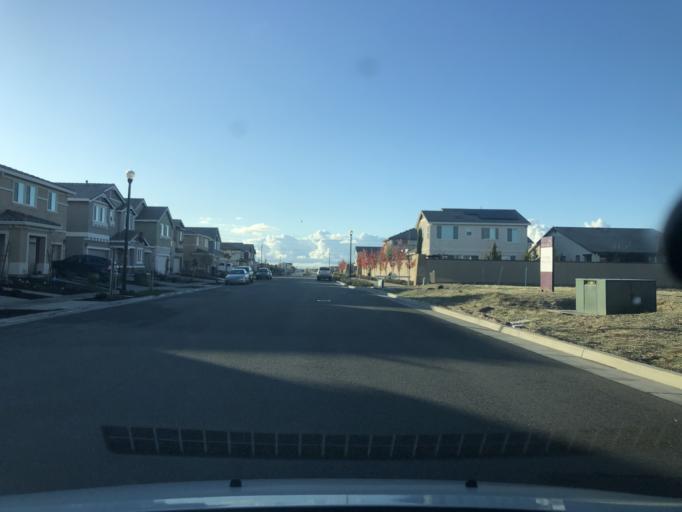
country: US
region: California
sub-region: Sacramento County
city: Antelope
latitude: 38.7710
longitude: -121.3818
